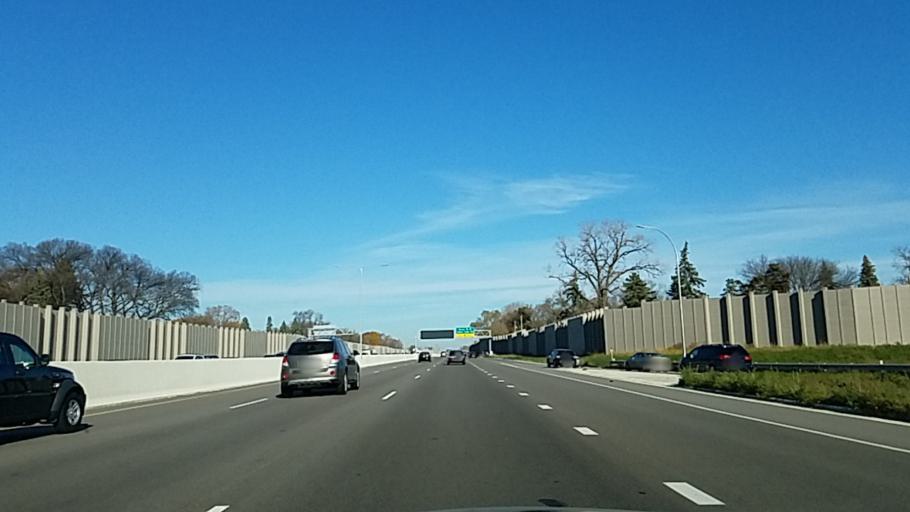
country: US
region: Minnesota
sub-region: Hennepin County
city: Saint Louis Park
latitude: 44.9499
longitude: -93.3475
